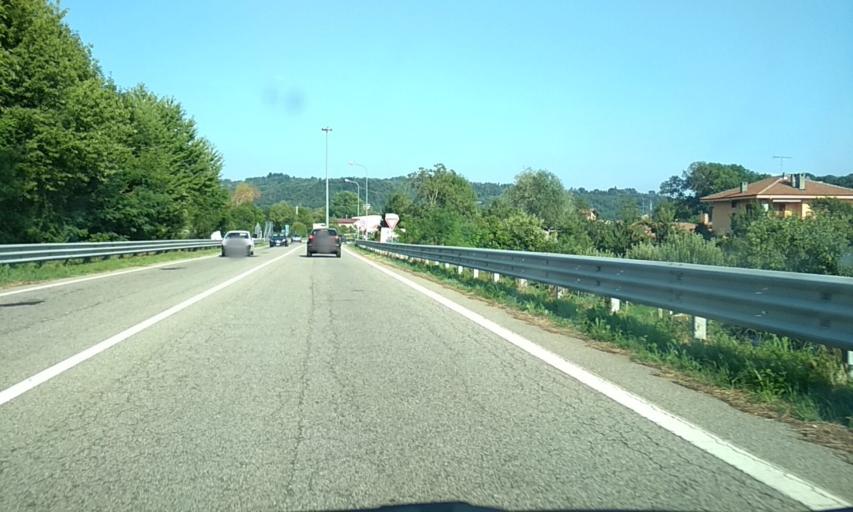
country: IT
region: Piedmont
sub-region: Provincia di Torino
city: Cuorgne
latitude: 45.4026
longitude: 7.6426
